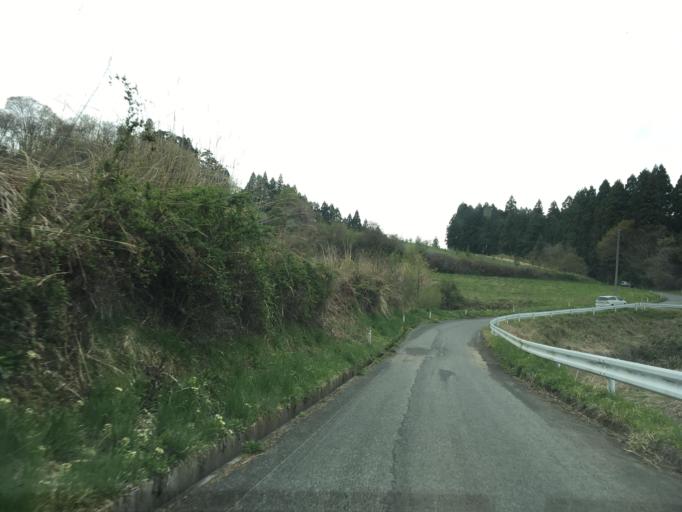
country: JP
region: Iwate
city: Ichinoseki
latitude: 38.8374
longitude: 141.3358
